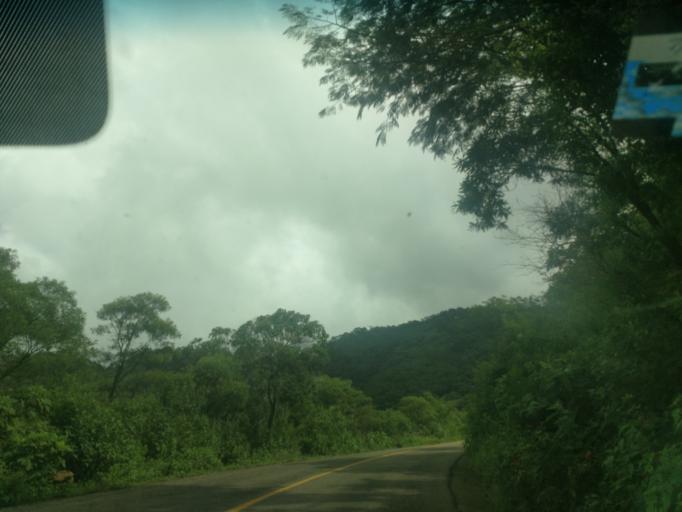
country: MX
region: Jalisco
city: El Salto
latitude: 20.3639
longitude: -104.5896
